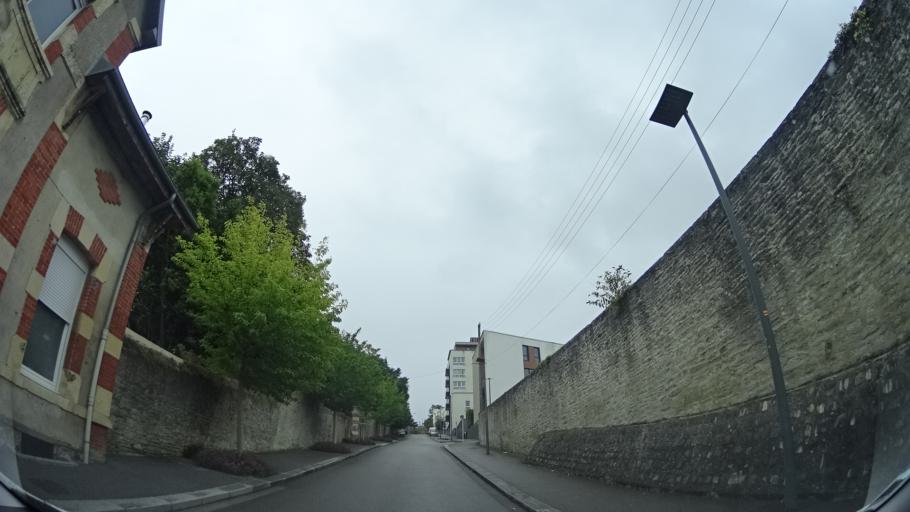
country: FR
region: Lower Normandy
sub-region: Departement de la Manche
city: Cherbourg-Octeville
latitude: 49.6325
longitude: -1.6211
